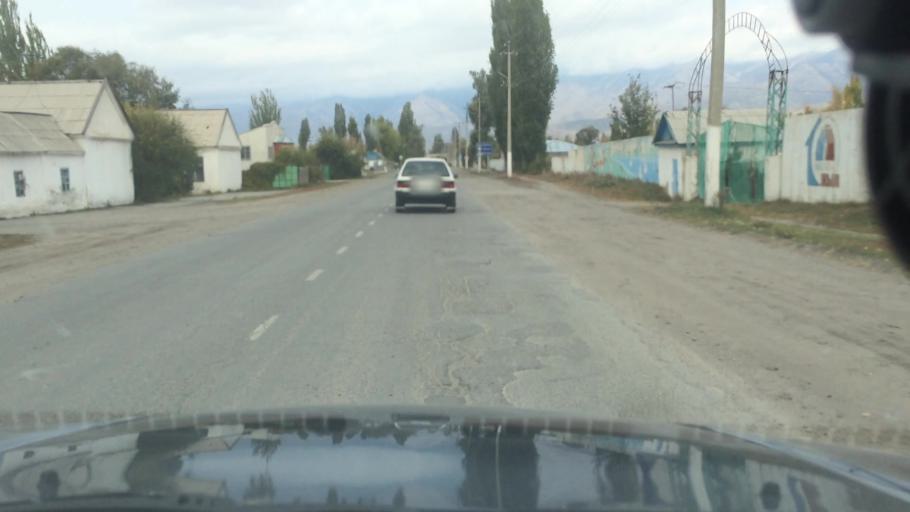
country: KG
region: Ysyk-Koel
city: Tyup
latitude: 42.7226
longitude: 78.3670
